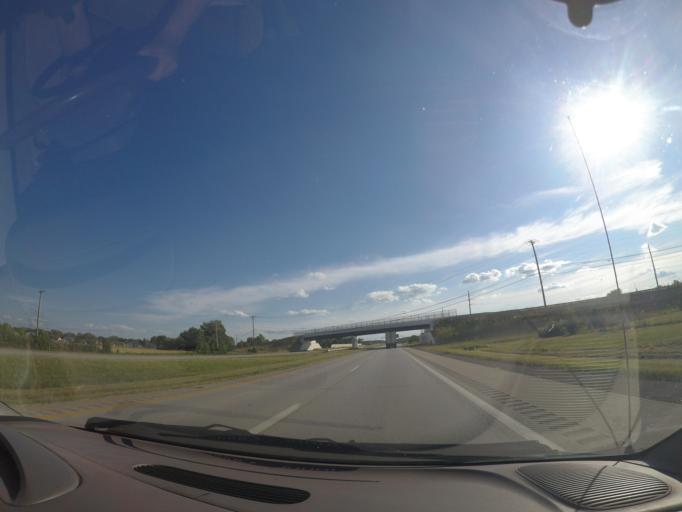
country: US
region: Ohio
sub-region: Henry County
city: Napoleon
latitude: 41.4023
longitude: -84.1404
